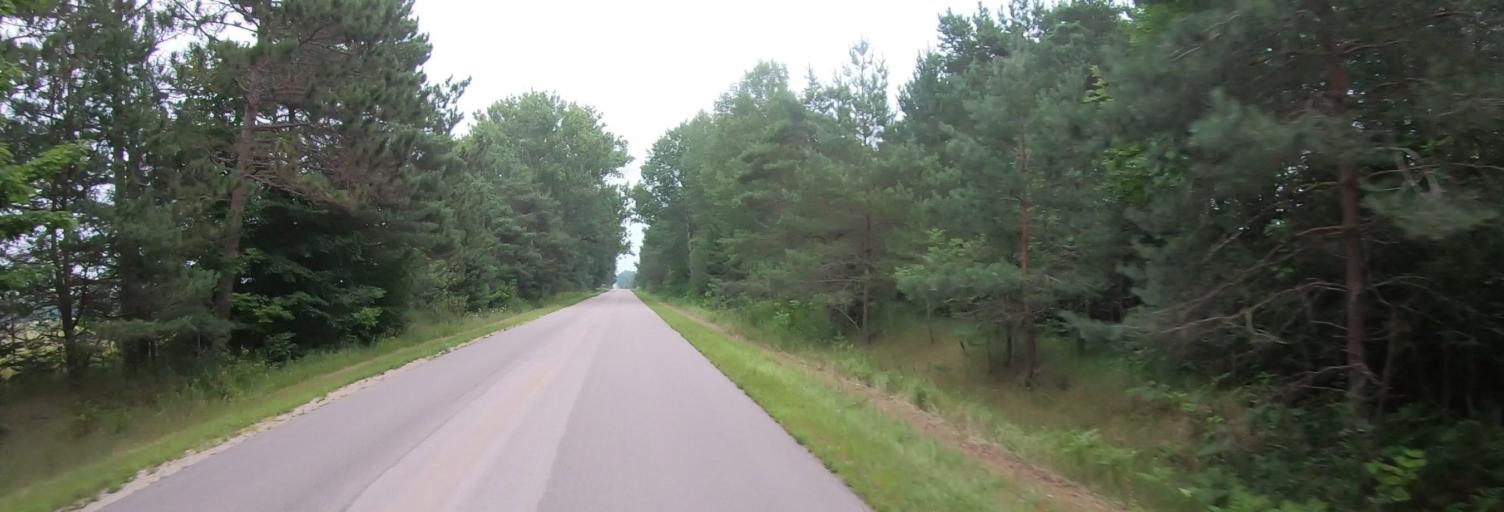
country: US
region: Michigan
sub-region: Mackinac County
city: Saint Ignace
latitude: 45.6944
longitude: -84.8170
